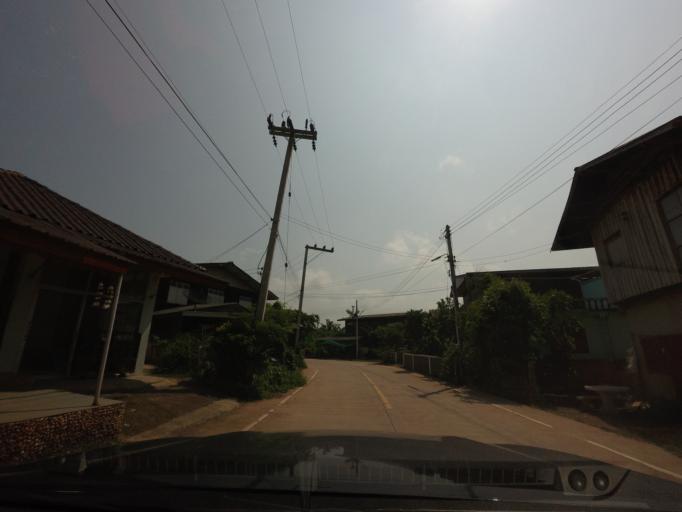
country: TH
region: Nan
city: Nan
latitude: 18.8610
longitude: 100.8129
